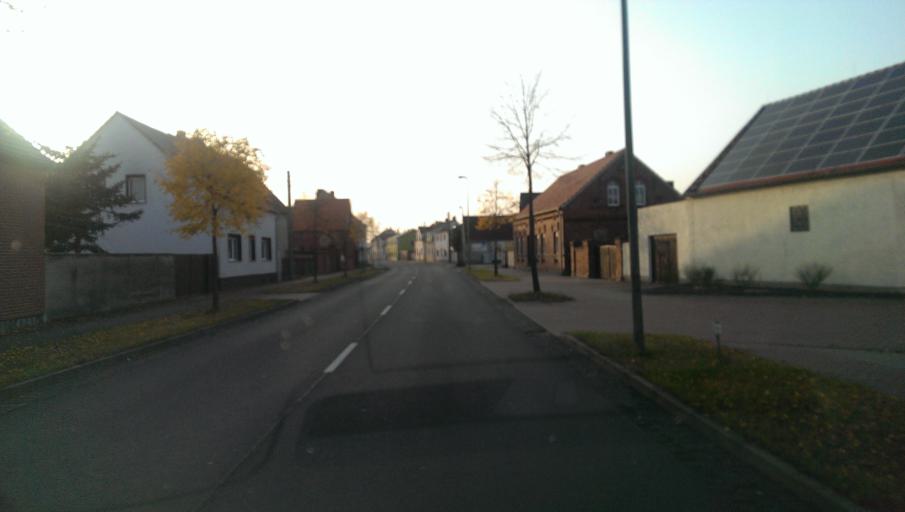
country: DE
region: Saxony-Anhalt
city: Holzdorf
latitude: 51.7790
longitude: 13.1258
